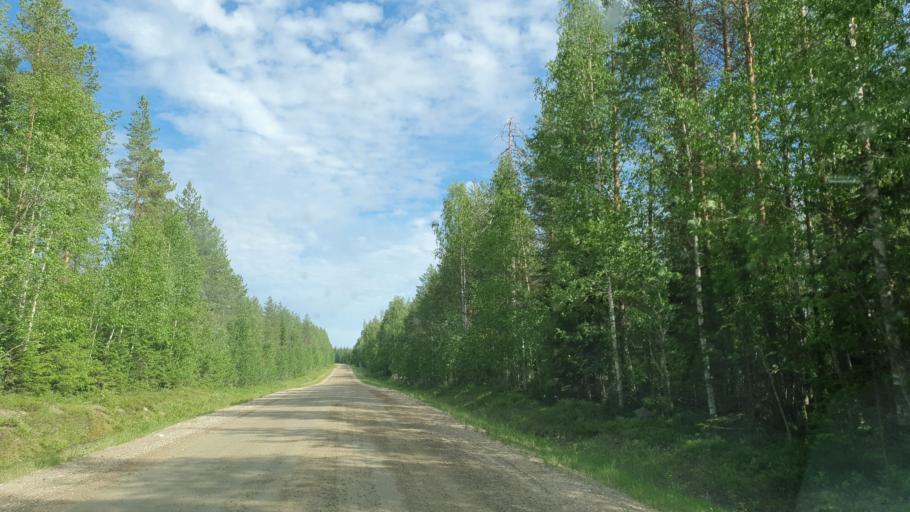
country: FI
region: Kainuu
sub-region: Kehys-Kainuu
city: Kuhmo
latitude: 64.5142
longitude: 29.4189
